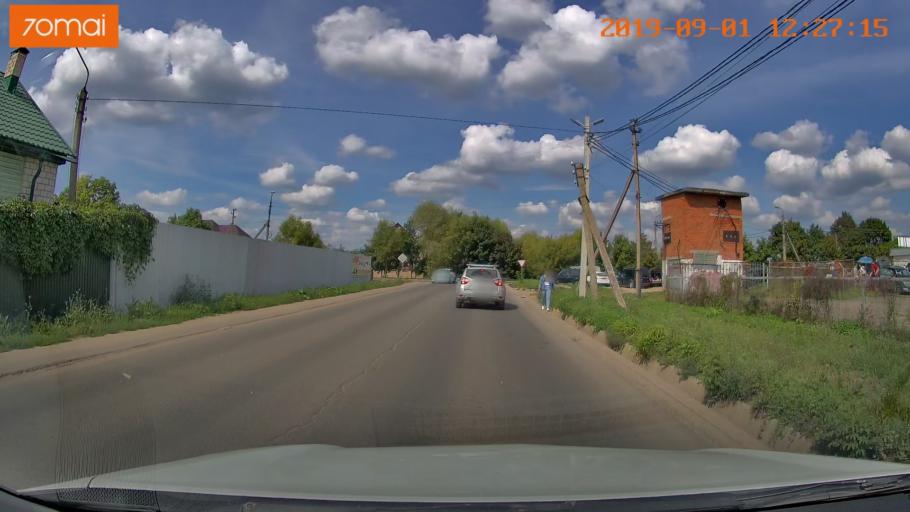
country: RU
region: Kaluga
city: Maloyaroslavets
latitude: 55.0053
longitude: 36.4597
